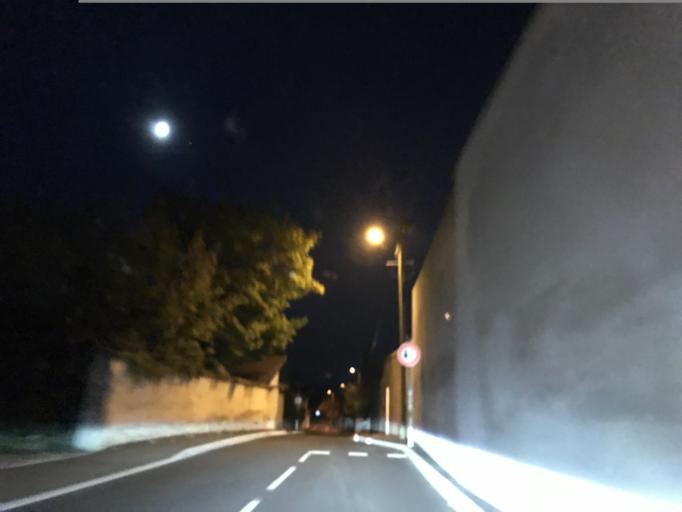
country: FR
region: Auvergne
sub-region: Departement du Puy-de-Dome
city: Thiers
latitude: 45.8630
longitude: 3.5309
